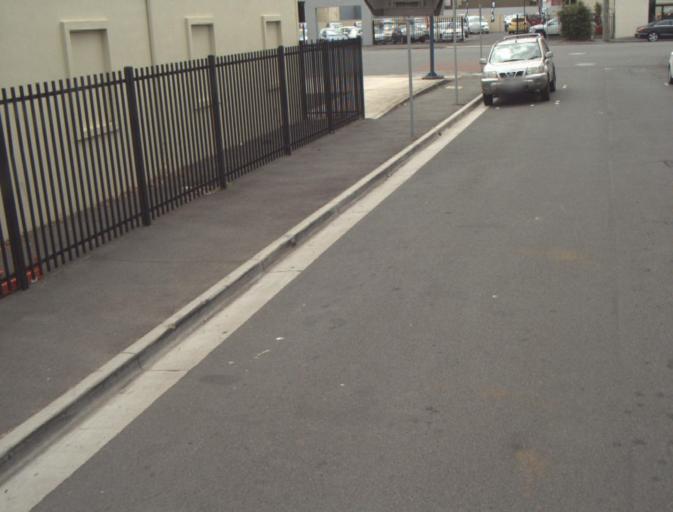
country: AU
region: Tasmania
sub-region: Launceston
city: Launceston
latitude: -41.4290
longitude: 147.1376
